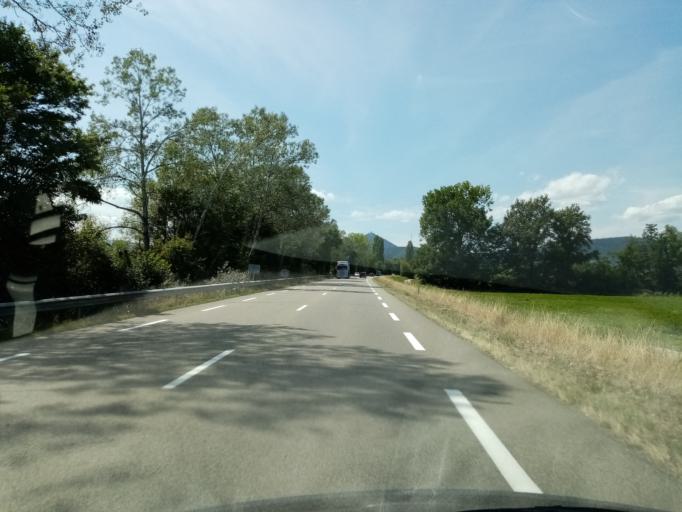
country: FR
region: Alsace
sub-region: Departement du Bas-Rhin
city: Selestat
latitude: 48.2477
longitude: 7.4473
